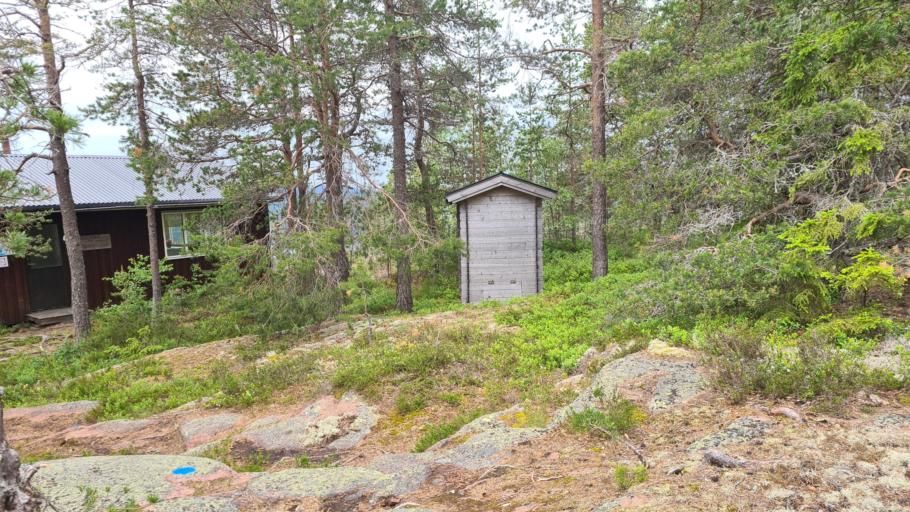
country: SE
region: Vaesternorrland
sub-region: Kramfors Kommun
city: Nordingra
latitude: 62.9737
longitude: 18.4443
